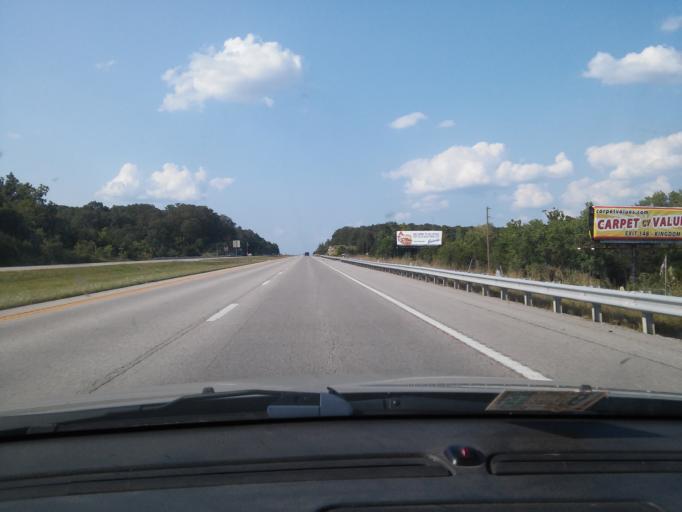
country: US
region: Missouri
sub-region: Cole County
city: Wardsville
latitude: 38.4899
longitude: -92.2702
